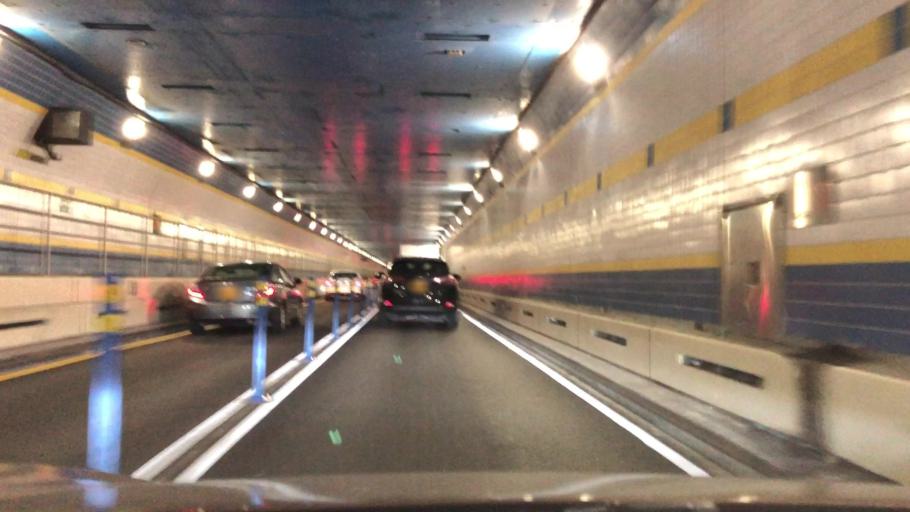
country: US
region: New York
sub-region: Queens County
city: Long Island City
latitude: 40.7457
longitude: -73.9651
